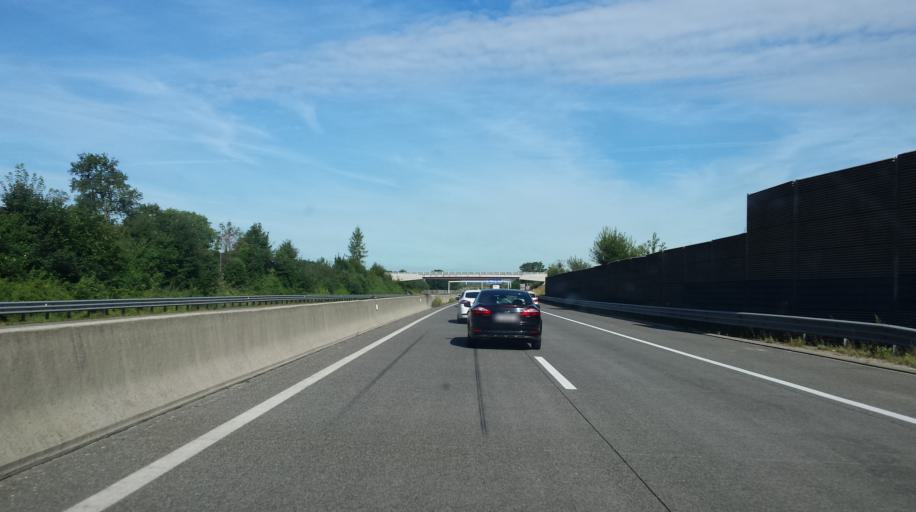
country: AT
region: Upper Austria
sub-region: Politischer Bezirk Vocklabruck
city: Aurach am Hongar
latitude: 47.9512
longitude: 13.6662
